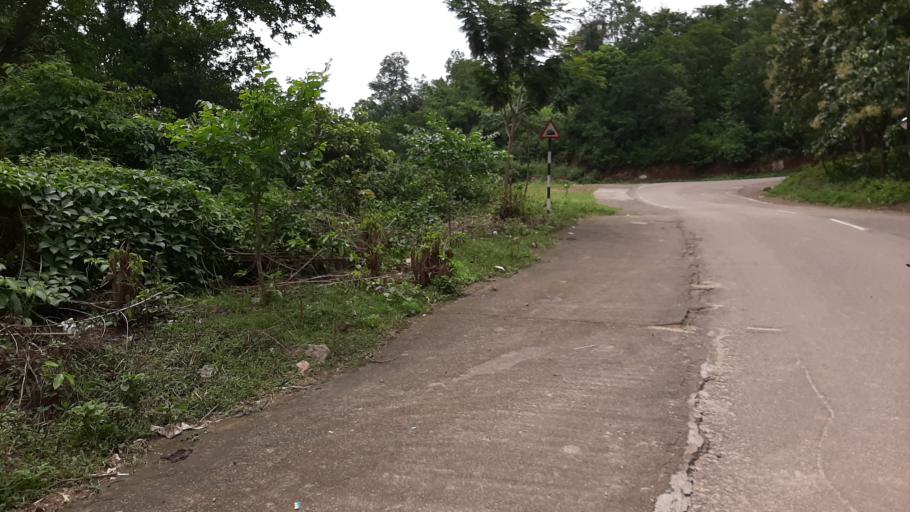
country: IN
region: Andhra Pradesh
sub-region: Vizianagaram District
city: Salur
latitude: 18.2764
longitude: 83.0375
